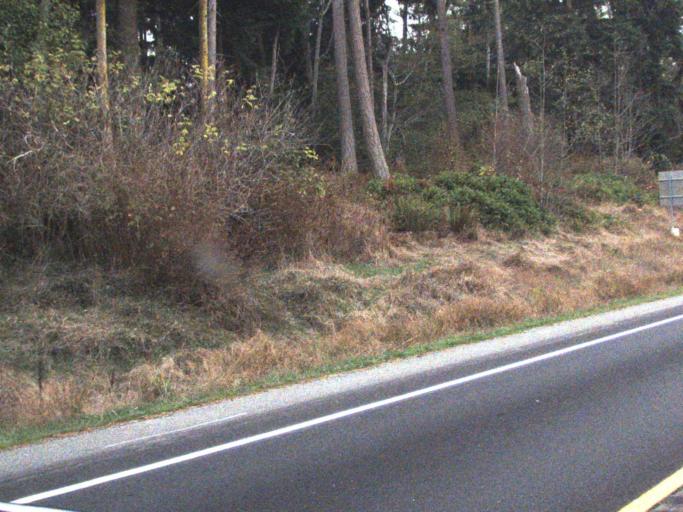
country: US
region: Washington
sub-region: Island County
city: Camano
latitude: 48.1303
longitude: -122.5899
